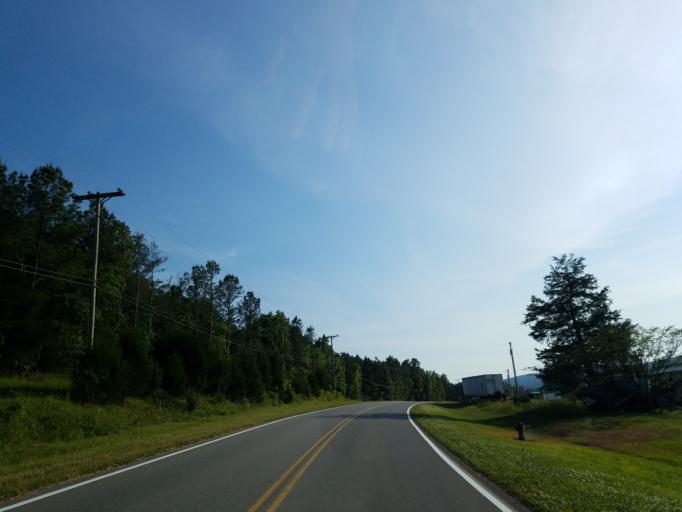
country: US
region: Georgia
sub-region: Chattooga County
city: Trion
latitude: 34.5119
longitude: -85.2320
